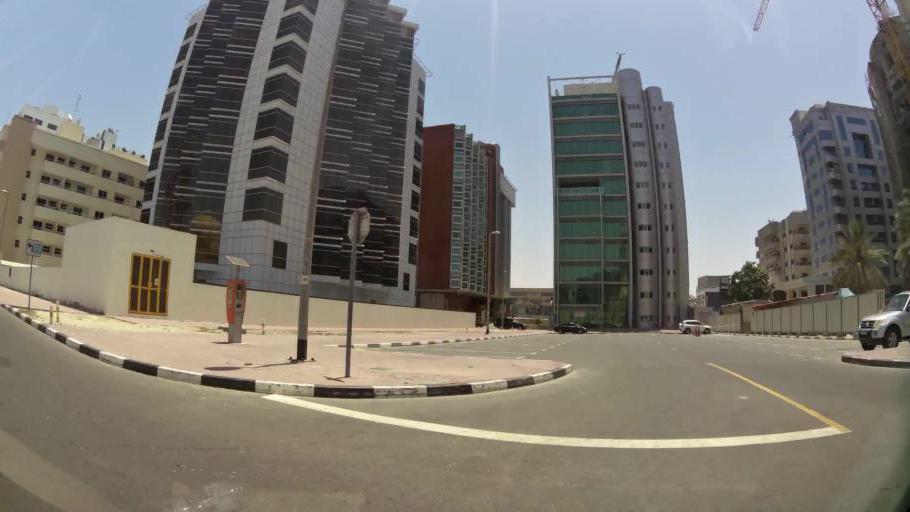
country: AE
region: Ash Shariqah
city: Sharjah
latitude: 25.2538
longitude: 55.3347
